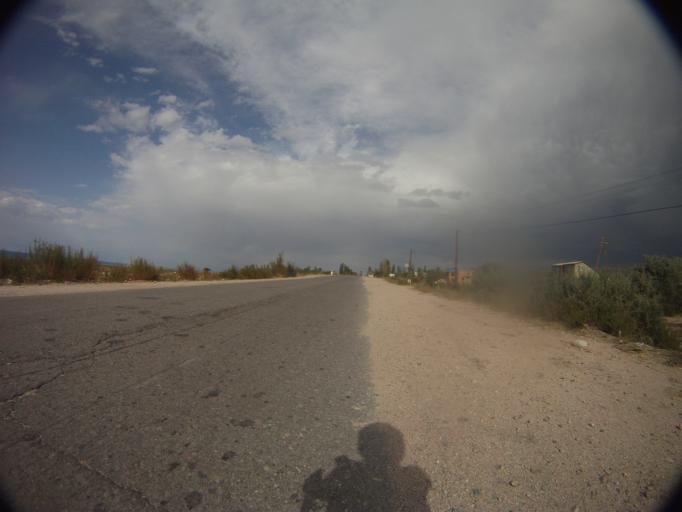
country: KG
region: Ysyk-Koel
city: Pokrovka
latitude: 42.2715
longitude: 77.7704
